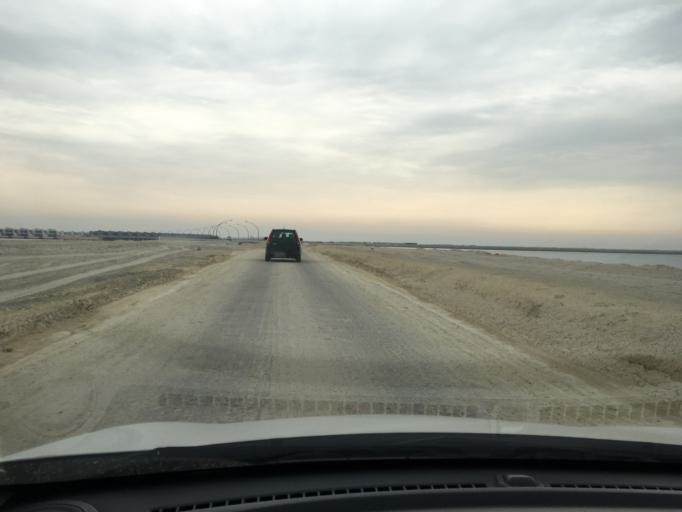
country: BH
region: Central Governorate
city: Dar Kulayb
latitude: 25.8302
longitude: 50.5959
